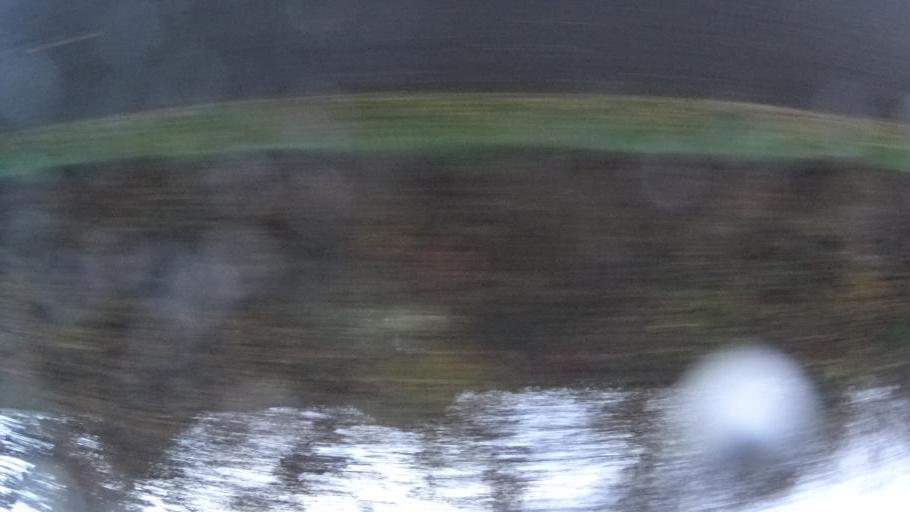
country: FR
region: Pays de la Loire
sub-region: Departement de la Loire-Atlantique
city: Avessac
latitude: 47.6700
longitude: -1.9864
